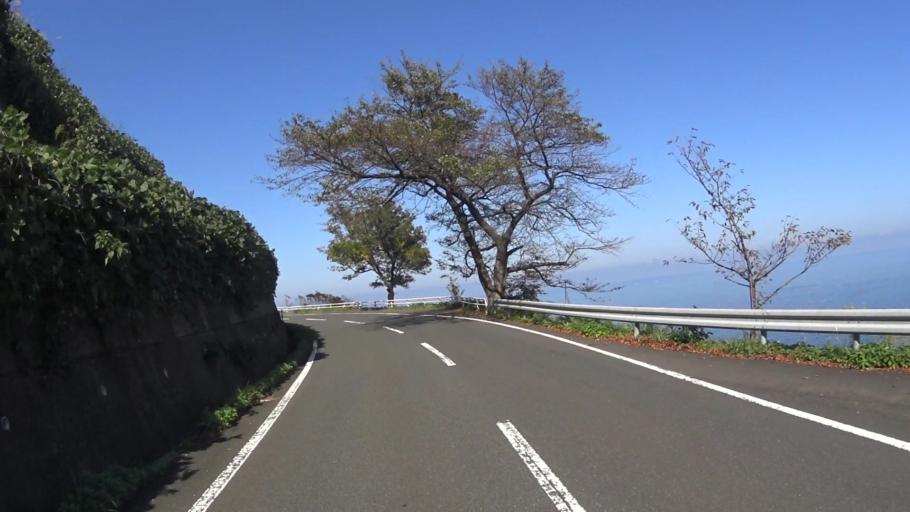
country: JP
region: Kyoto
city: Miyazu
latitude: 35.7579
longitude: 135.2446
